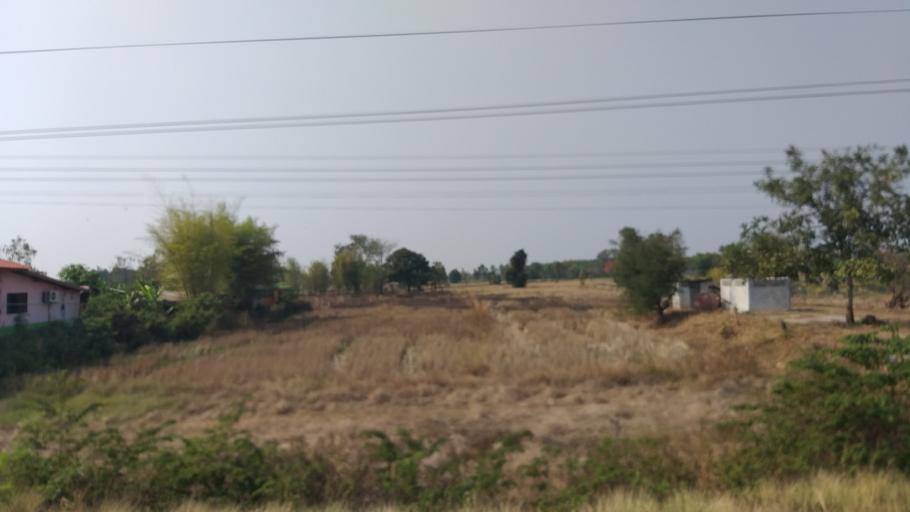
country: TH
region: Changwat Udon Thani
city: Nong Han
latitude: 17.3700
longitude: 103.1805
